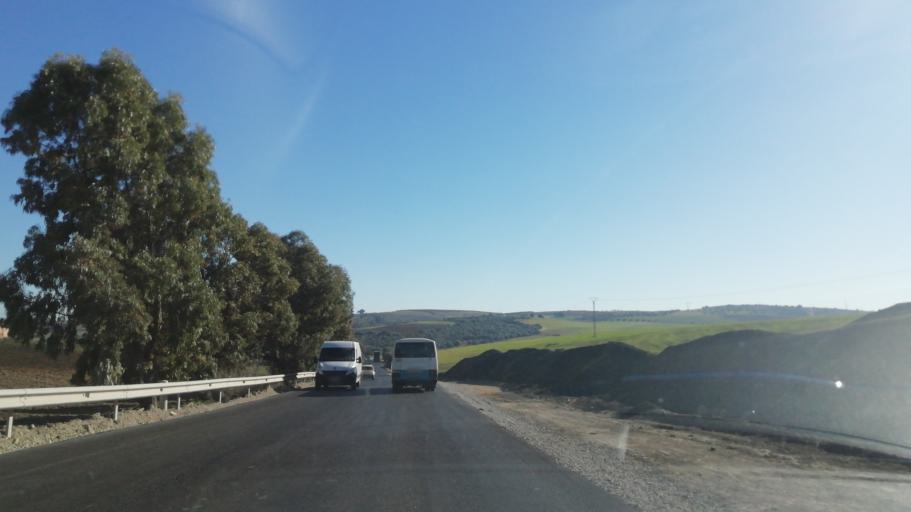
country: DZ
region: Relizane
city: Smala
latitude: 35.6728
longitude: 0.8042
